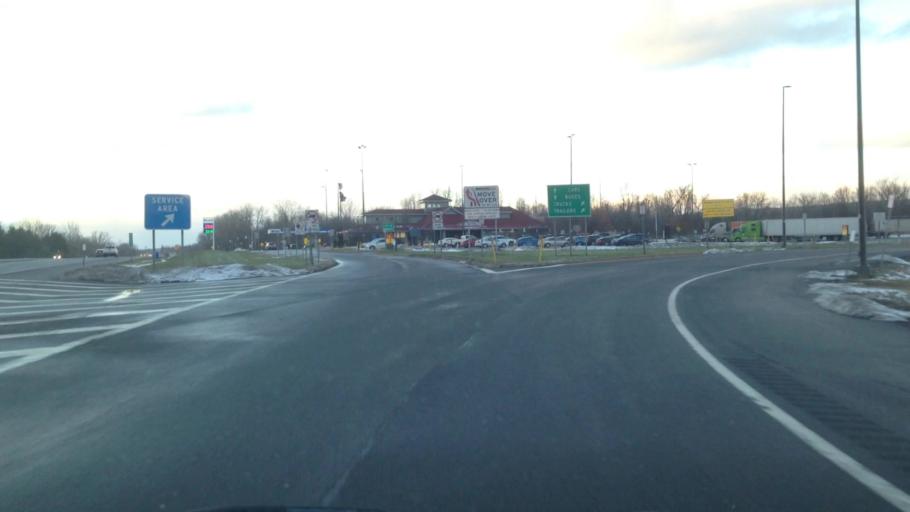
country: US
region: New York
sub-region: Herkimer County
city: Frankfort
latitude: 43.0750
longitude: -75.1017
